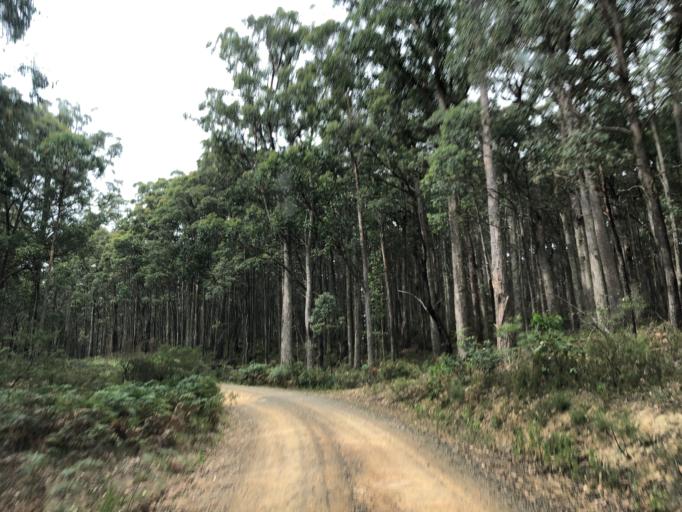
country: AU
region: Victoria
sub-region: Moorabool
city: Bacchus Marsh
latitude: -37.4417
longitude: 144.3434
